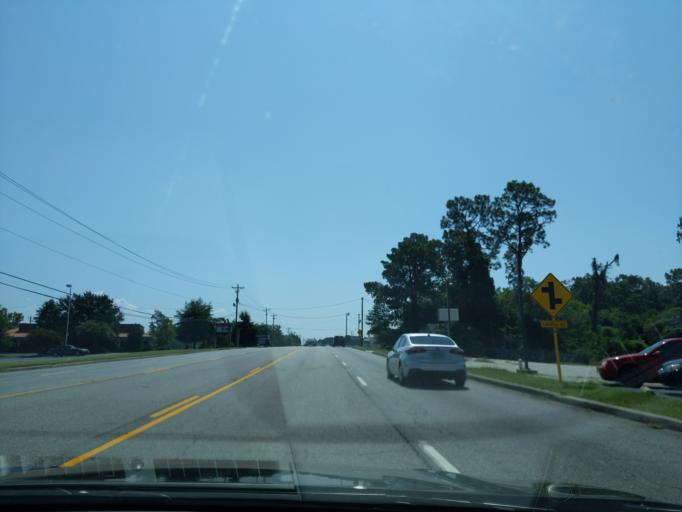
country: US
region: South Carolina
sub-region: Lexington County
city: Oak Grove
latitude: 33.9761
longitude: -81.1807
